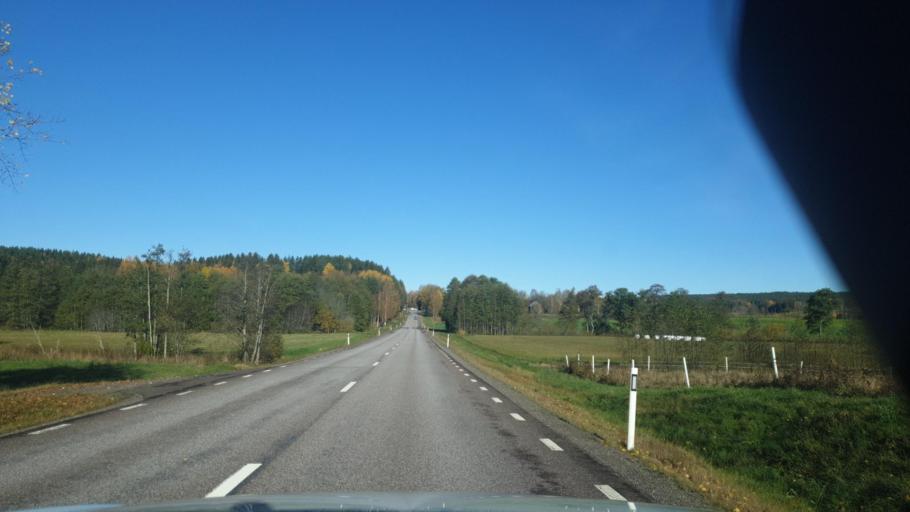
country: SE
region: Vaermland
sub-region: Arvika Kommun
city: Arvika
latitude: 59.4668
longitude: 12.7739
